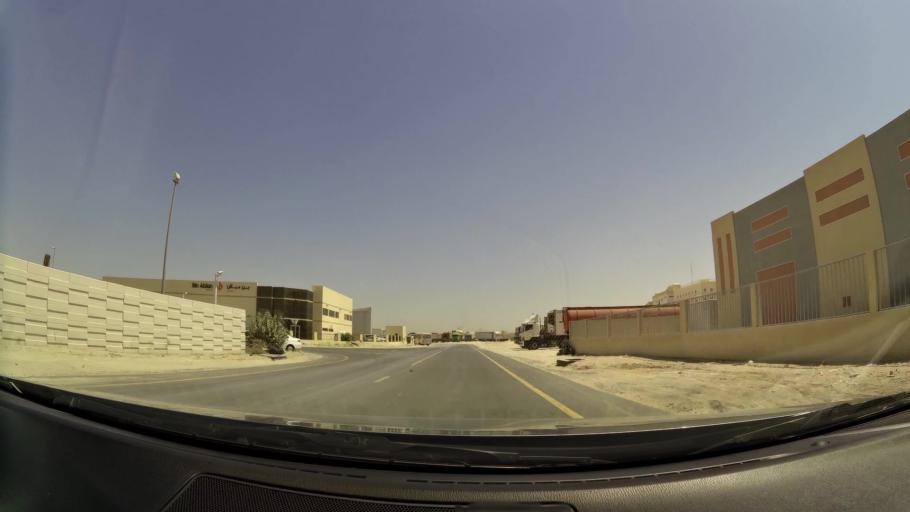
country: AE
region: Dubai
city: Dubai
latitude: 24.9762
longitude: 55.1990
